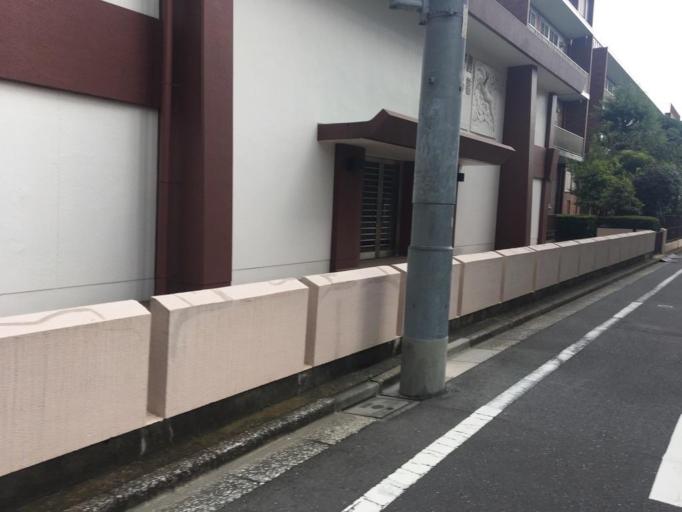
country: JP
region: Tokyo
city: Tokyo
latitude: 35.7290
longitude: 139.7368
